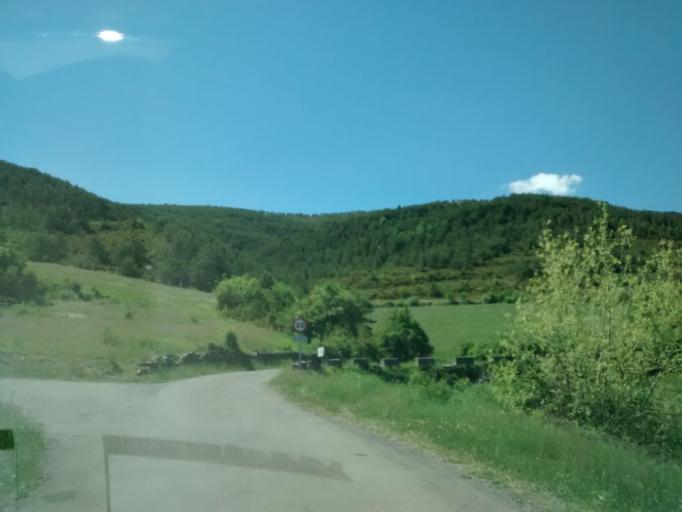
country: ES
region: Aragon
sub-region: Provincia de Huesca
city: Jasa
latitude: 42.6907
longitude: -0.6212
